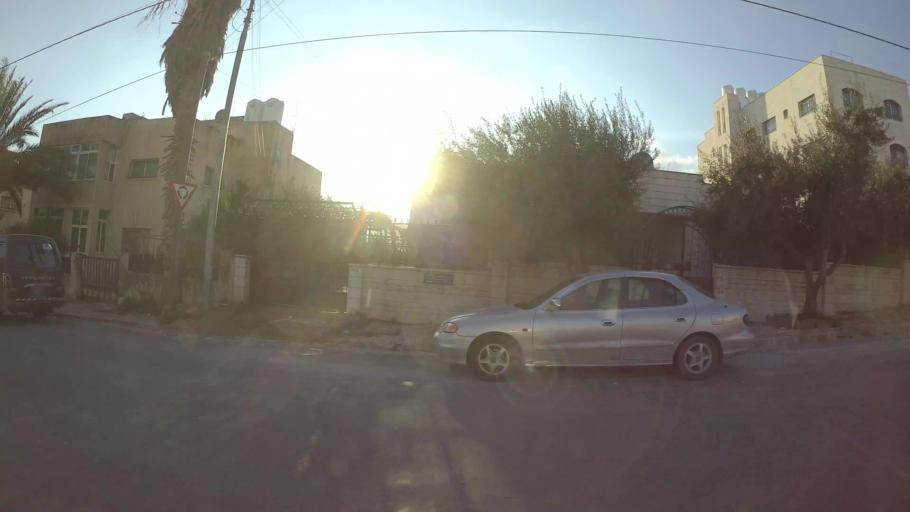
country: JO
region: Amman
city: Al Bunayyat ash Shamaliyah
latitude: 31.8981
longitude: 35.9091
